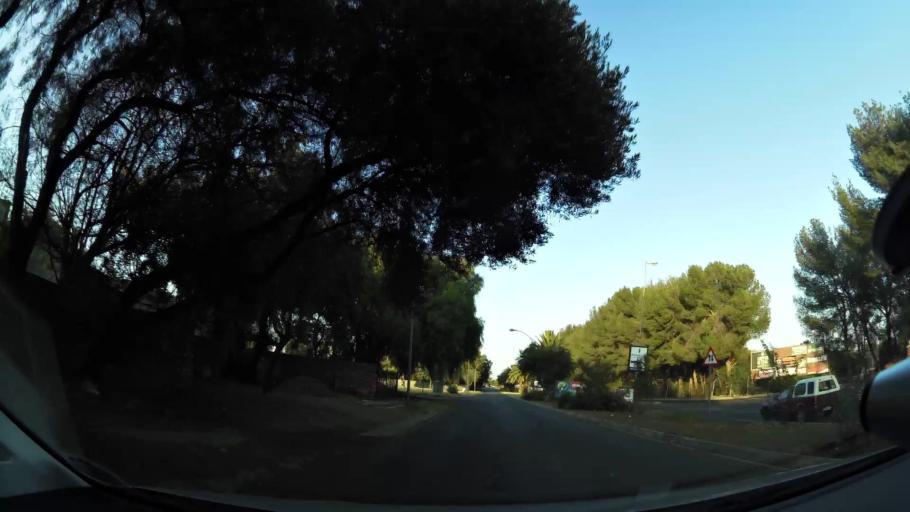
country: ZA
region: Orange Free State
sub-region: Mangaung Metropolitan Municipality
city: Bloemfontein
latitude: -29.0842
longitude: 26.1569
